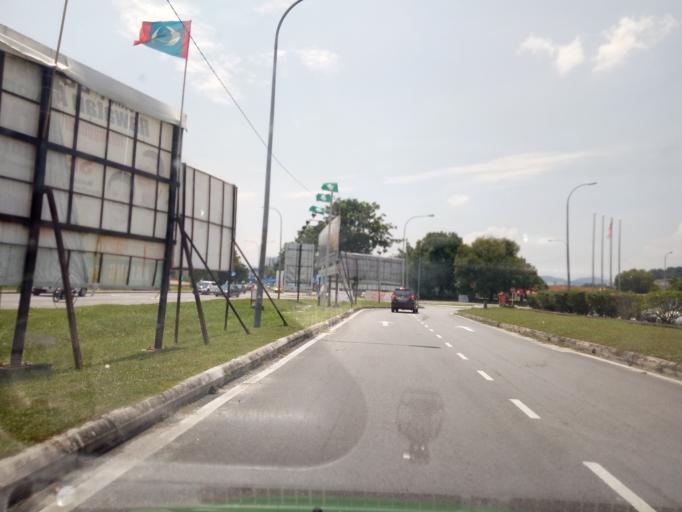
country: MY
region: Selangor
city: Kampong Baharu Balakong
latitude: 3.0049
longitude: 101.7851
